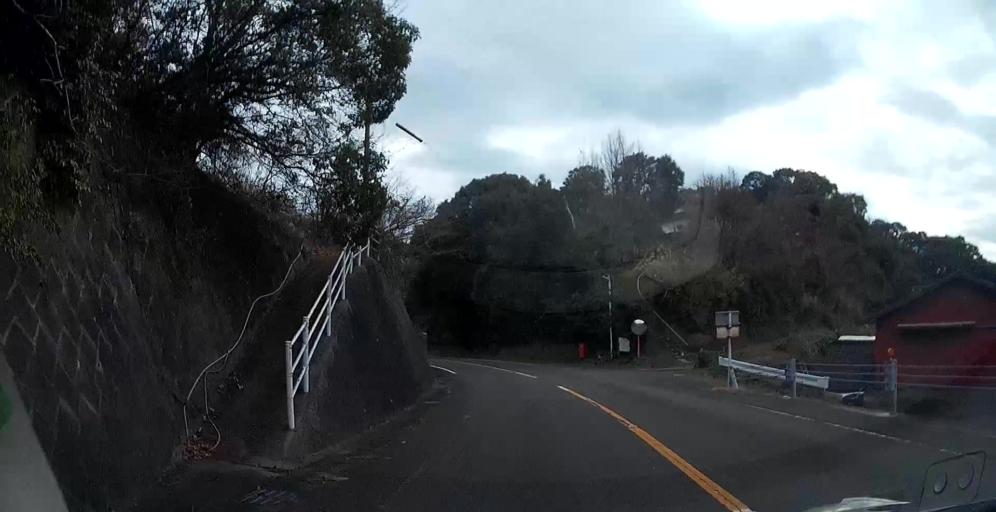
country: JP
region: Kumamoto
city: Minamata
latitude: 32.3633
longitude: 130.4944
